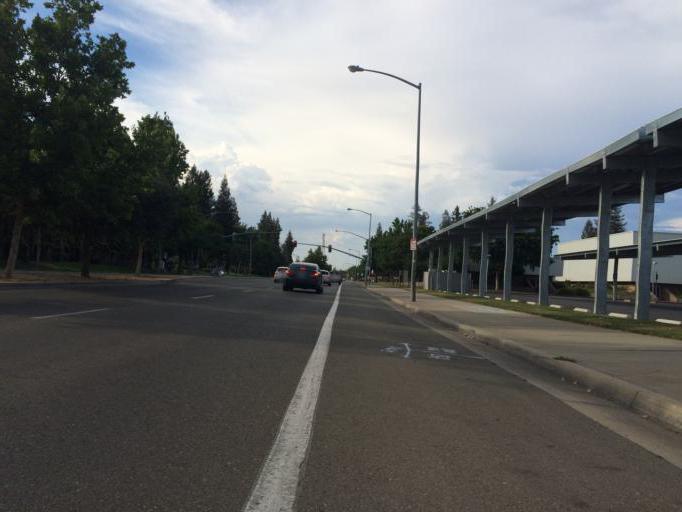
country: US
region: California
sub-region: Fresno County
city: Clovis
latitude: 36.8473
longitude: -119.7745
